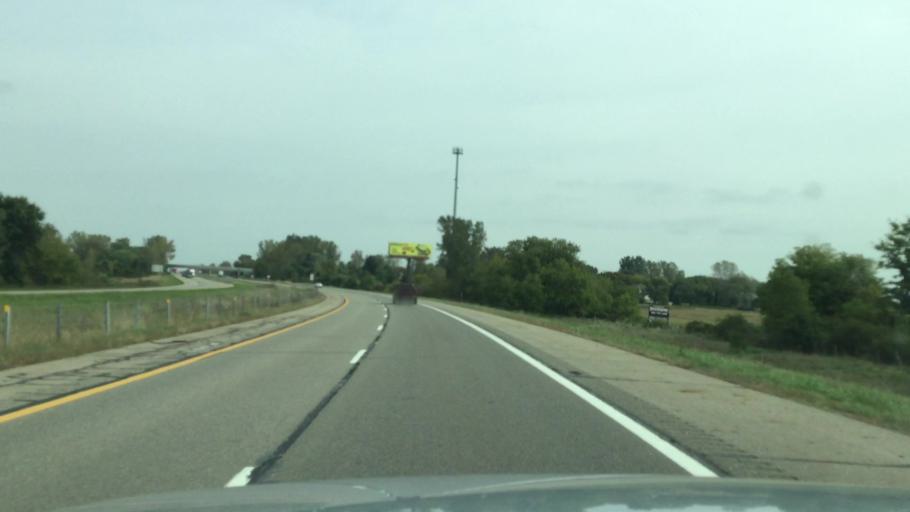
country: US
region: Michigan
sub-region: Shiawassee County
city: Durand
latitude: 42.9297
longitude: -83.9934
